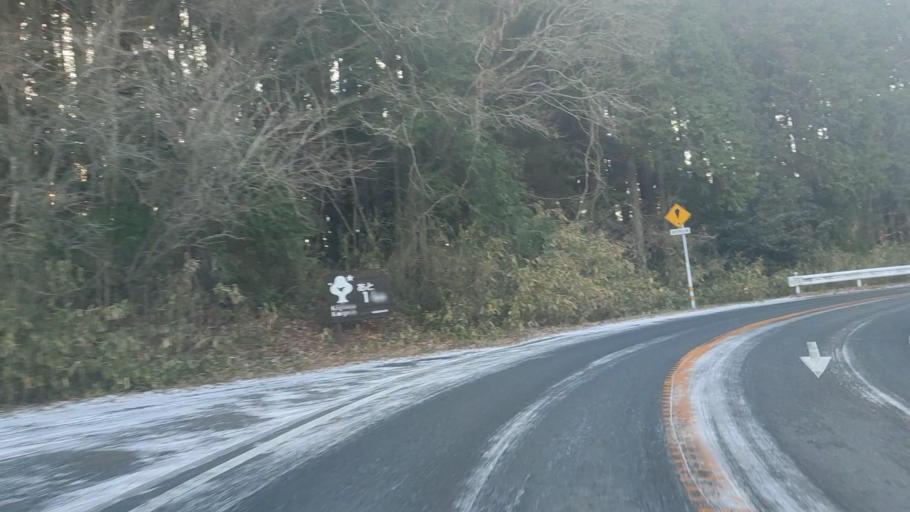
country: JP
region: Oita
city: Beppu
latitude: 33.2680
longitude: 131.4318
